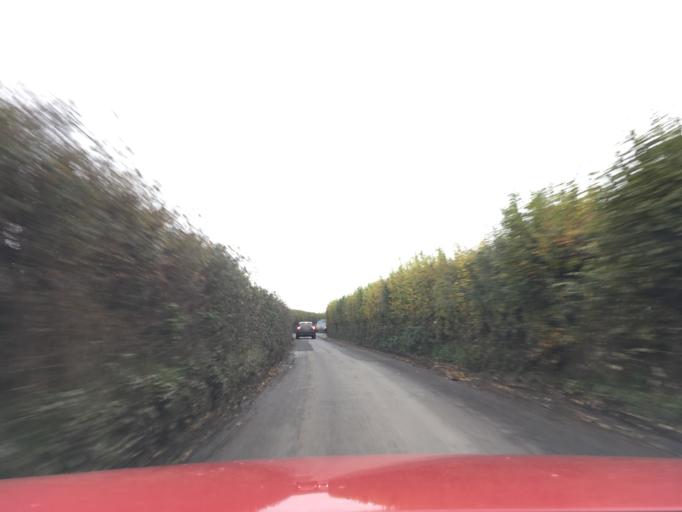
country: GB
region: England
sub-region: Somerset
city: South Petherton
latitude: 50.9348
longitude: -2.8295
